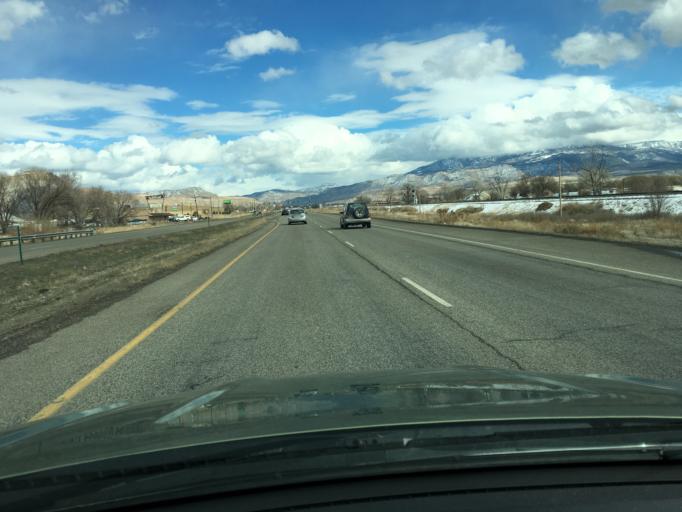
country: US
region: Colorado
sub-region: Mesa County
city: Fruitvale
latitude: 39.0819
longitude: -108.4777
